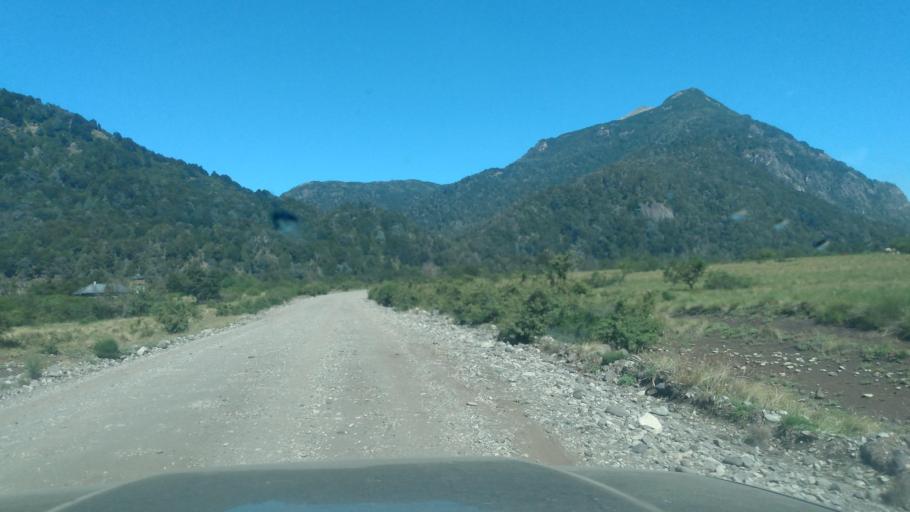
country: AR
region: Neuquen
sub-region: Departamento de Lacar
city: San Martin de los Andes
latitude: -39.7459
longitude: -71.5182
